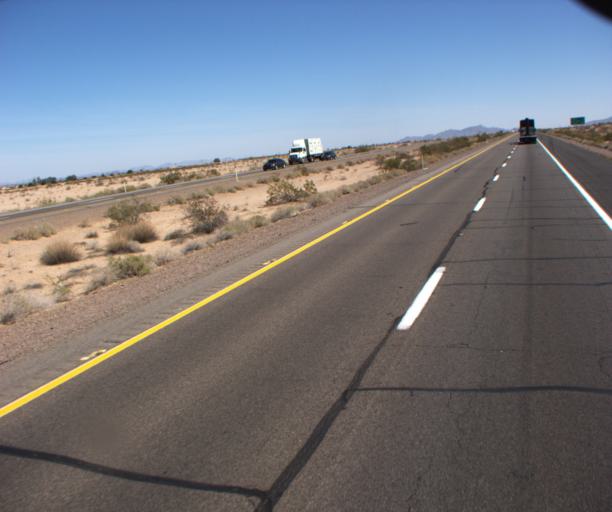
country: US
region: Arizona
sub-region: Yuma County
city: Wellton
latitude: 32.6843
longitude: -114.0080
